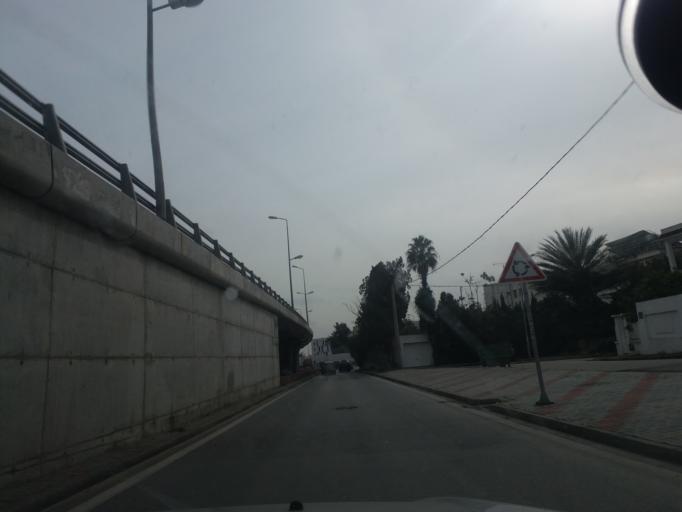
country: TN
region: Tunis
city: Tunis
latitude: 36.8334
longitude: 10.1792
